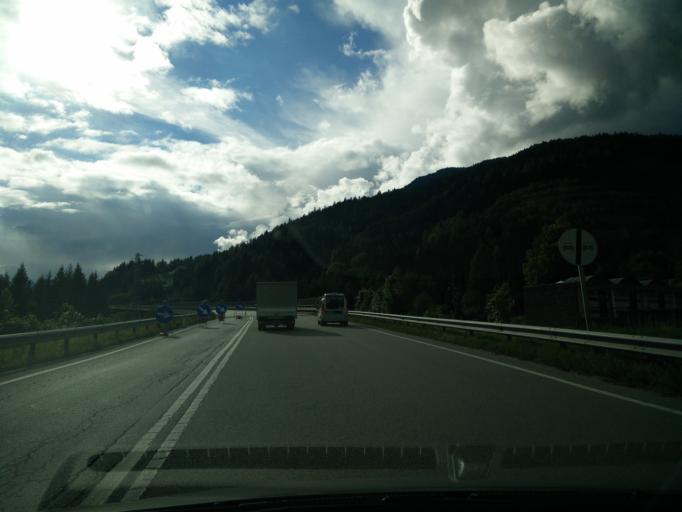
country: IT
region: Veneto
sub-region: Provincia di Belluno
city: Lozzo di Cadore
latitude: 46.4832
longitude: 12.4457
